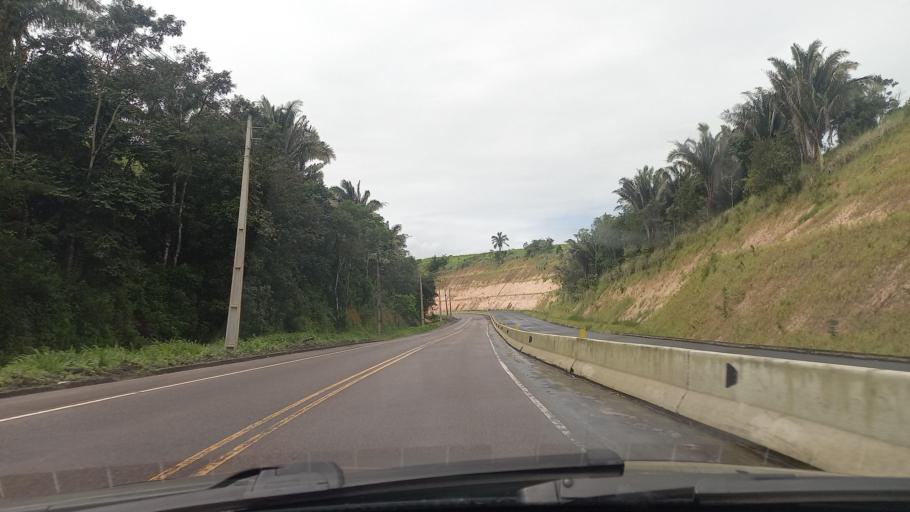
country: BR
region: Alagoas
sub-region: Campo Alegre
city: Campo Alegre
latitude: -9.8217
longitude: -36.2279
